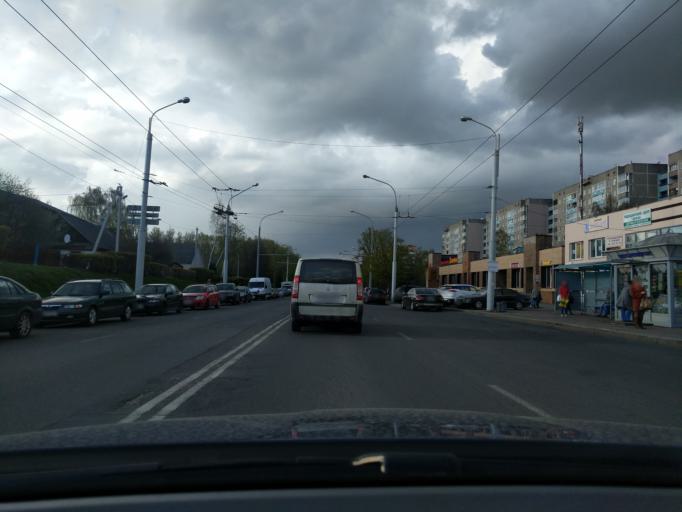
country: BY
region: Minsk
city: Novoye Medvezhino
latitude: 53.8947
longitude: 27.4813
